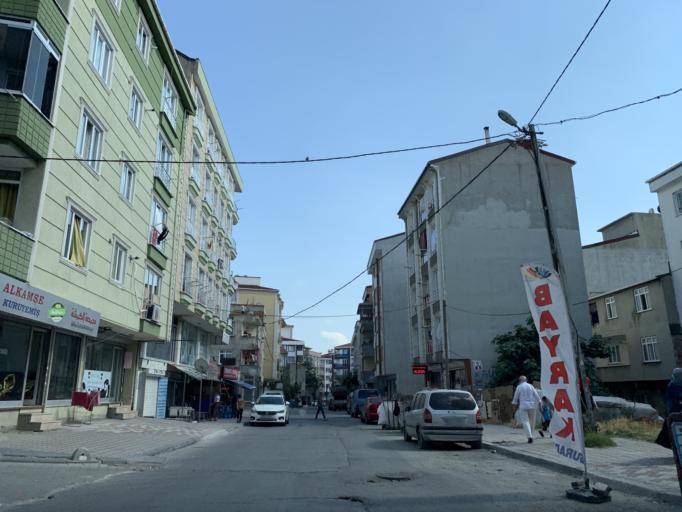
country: TR
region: Istanbul
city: Esenyurt
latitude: 41.0366
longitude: 28.6754
